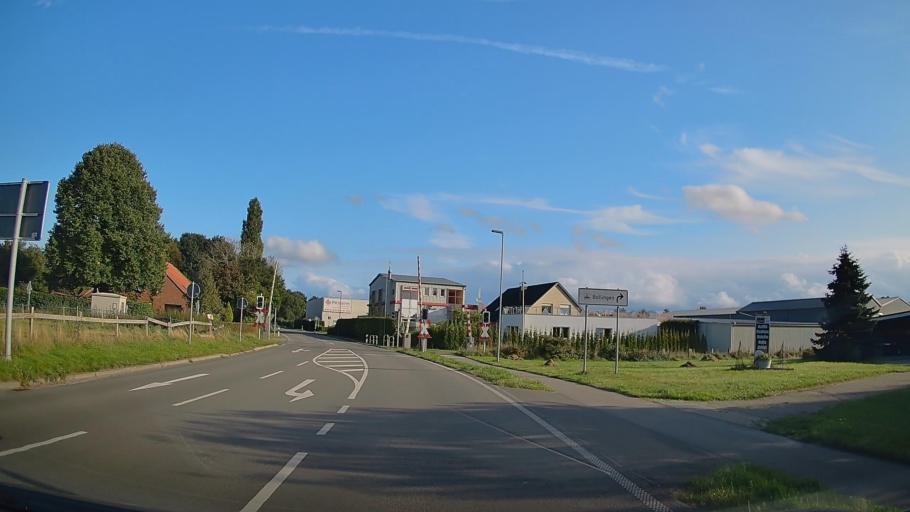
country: DE
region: Lower Saxony
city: Barssel
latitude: 53.1326
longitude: 7.6822
